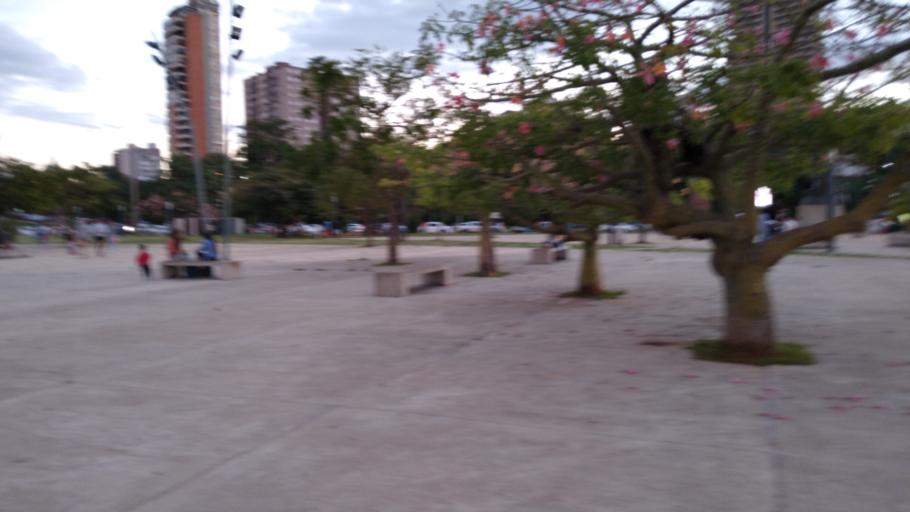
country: AR
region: Misiones
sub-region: Departamento de Capital
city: Posadas
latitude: -27.3617
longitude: -55.8857
